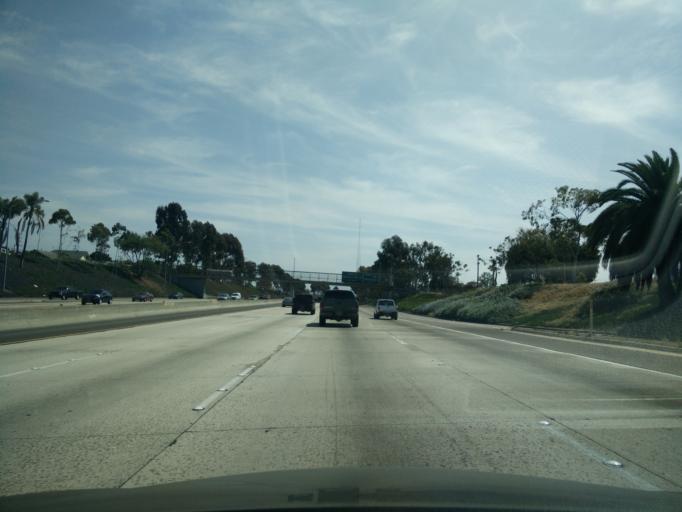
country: US
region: California
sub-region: San Diego County
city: San Diego
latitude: 32.6943
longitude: -117.1312
